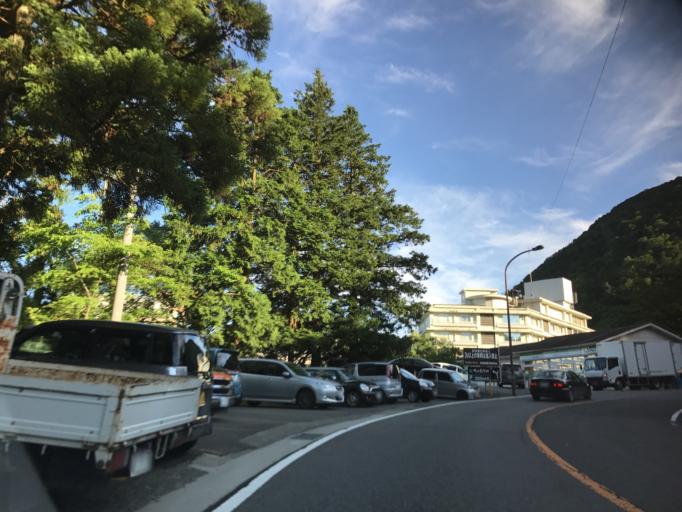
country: JP
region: Kanagawa
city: Hakone
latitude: 35.2400
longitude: 139.0475
